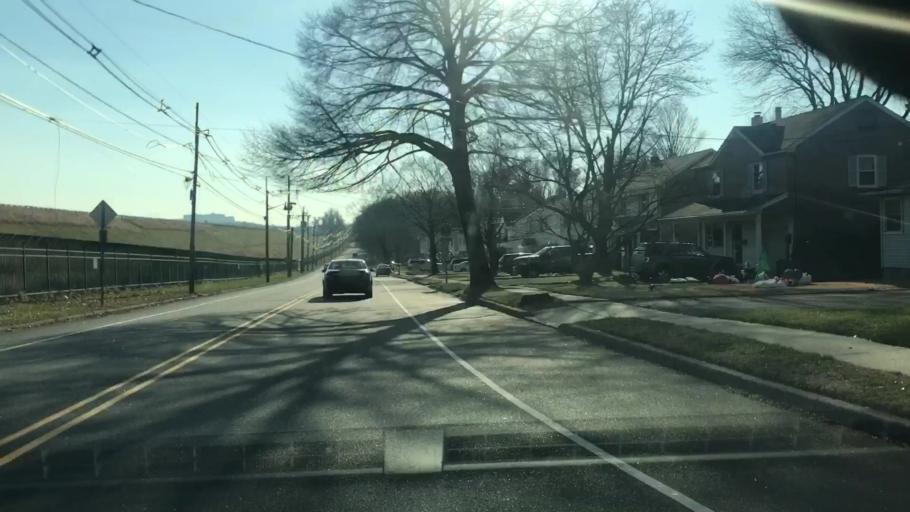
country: US
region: New Jersey
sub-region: Passaic County
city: Little Falls
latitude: 40.8645
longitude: -74.2131
